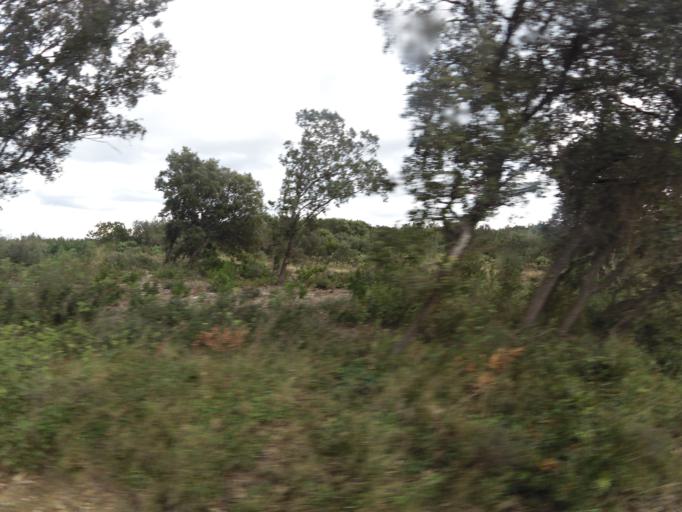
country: FR
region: Languedoc-Roussillon
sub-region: Departement du Gard
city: Clarensac
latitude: 43.8421
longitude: 4.1907
